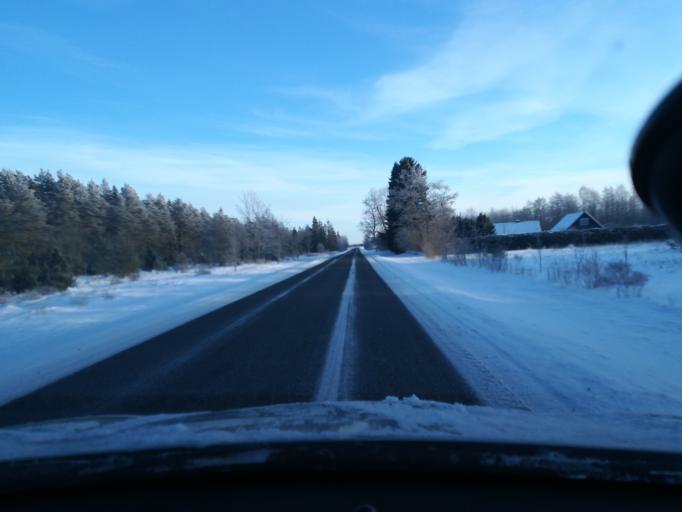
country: EE
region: Harju
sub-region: Keila linn
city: Keila
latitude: 59.3964
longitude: 24.3710
